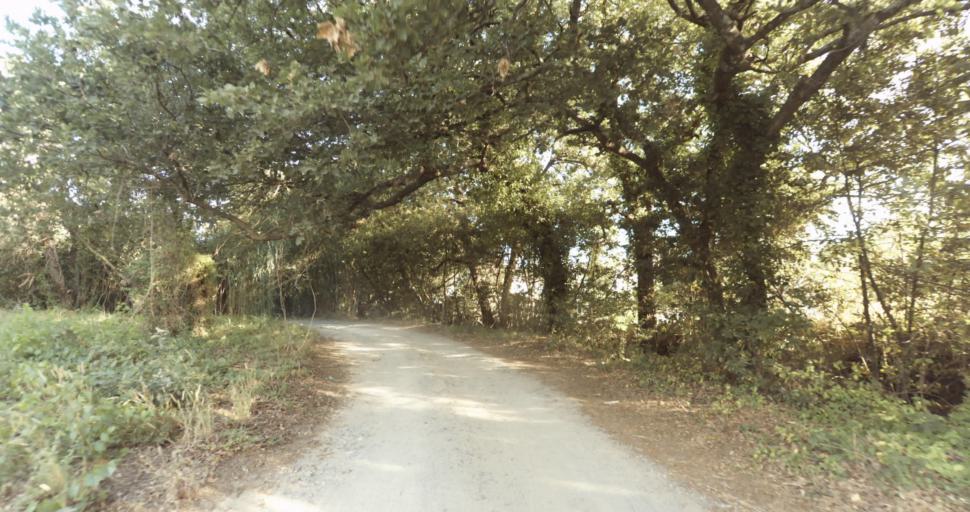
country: FR
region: Provence-Alpes-Cote d'Azur
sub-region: Departement du Var
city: Saint-Tropez
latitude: 43.2557
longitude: 6.6359
